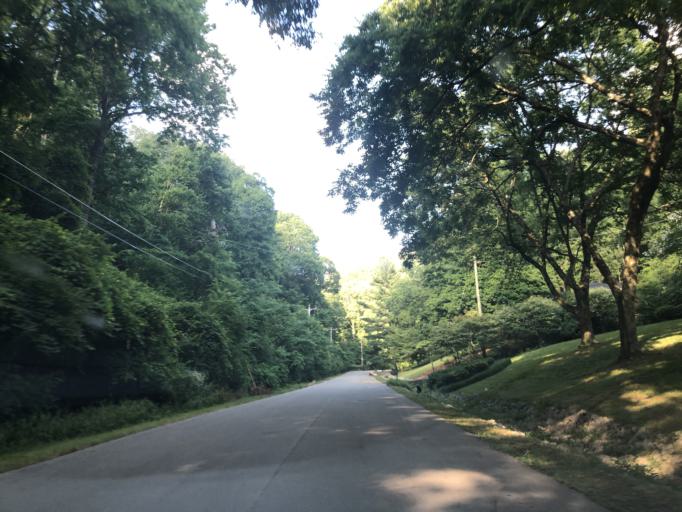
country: US
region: Tennessee
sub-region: Davidson County
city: Forest Hills
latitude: 36.0703
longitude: -86.8221
